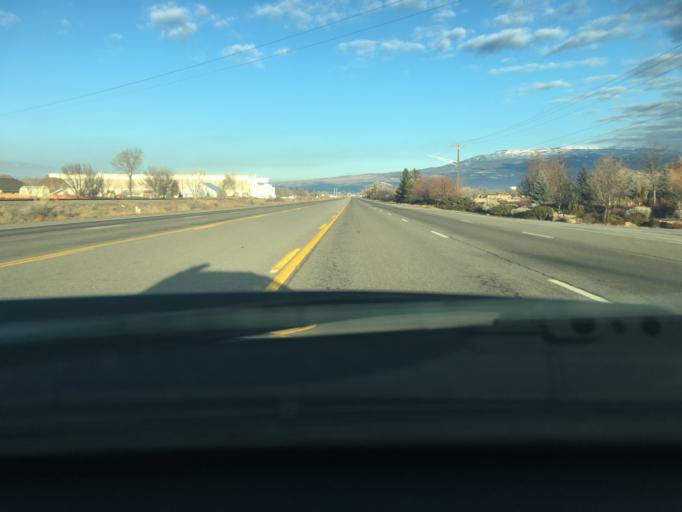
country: US
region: Colorado
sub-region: Delta County
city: Delta
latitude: 38.7203
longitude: -108.0586
